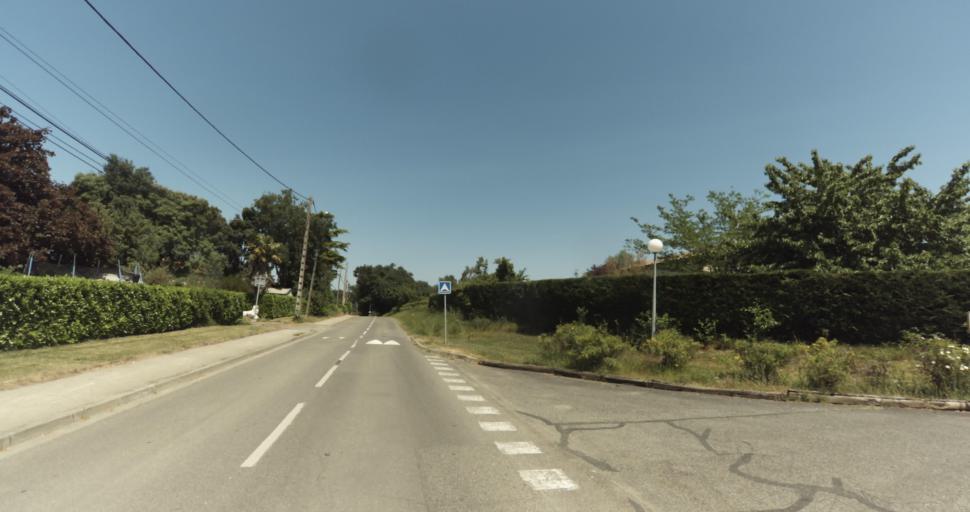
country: FR
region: Midi-Pyrenees
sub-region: Departement de la Haute-Garonne
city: Levignac
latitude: 43.6392
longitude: 1.1715
